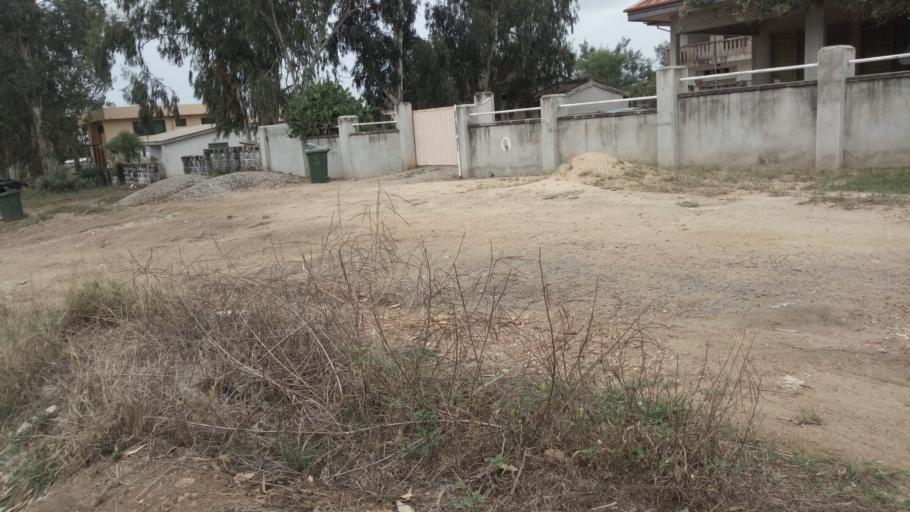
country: GH
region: Central
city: Winneba
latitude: 5.3672
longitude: -0.6383
